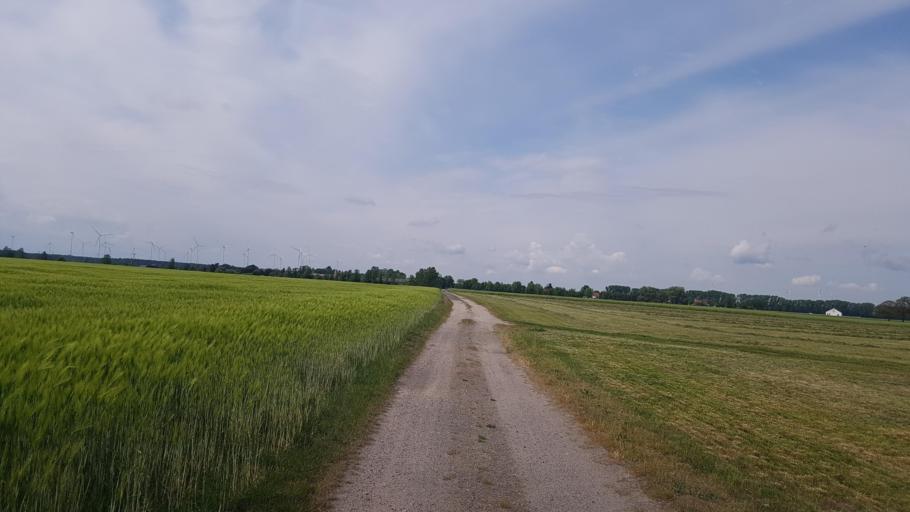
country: DE
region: Brandenburg
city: Sallgast
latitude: 51.5984
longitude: 13.8665
